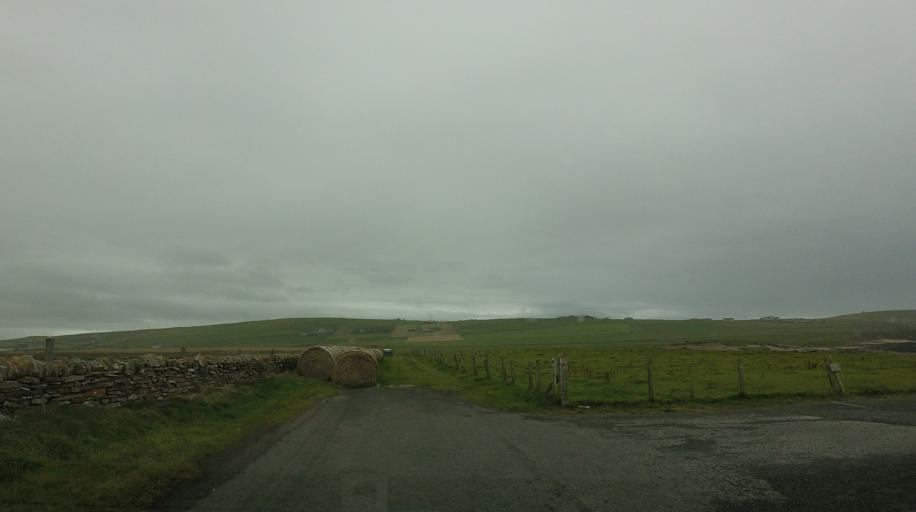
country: GB
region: Scotland
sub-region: Orkney Islands
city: Stromness
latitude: 59.1258
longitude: -3.3155
